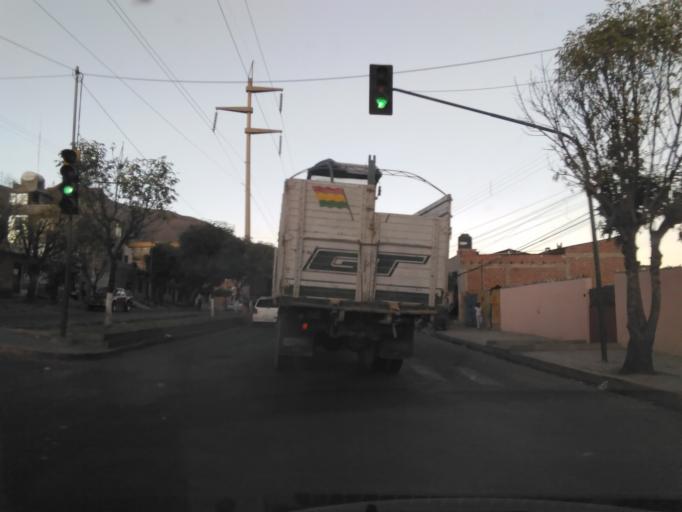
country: BO
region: Cochabamba
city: Cochabamba
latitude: -17.3728
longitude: -66.1352
